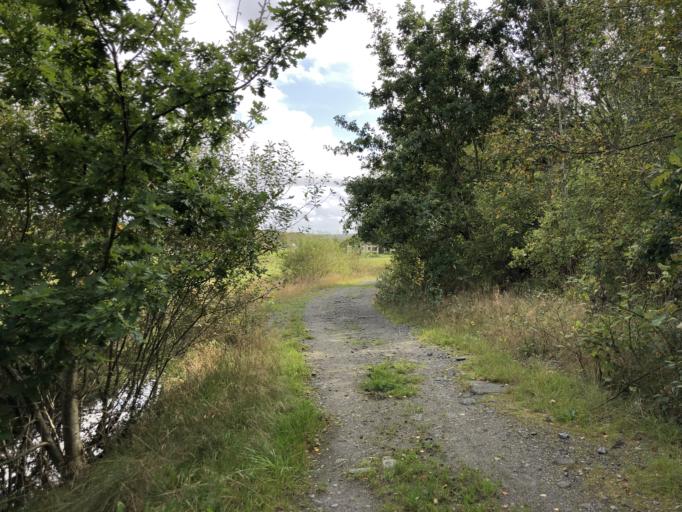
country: SE
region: Vaestra Goetaland
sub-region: Goteborg
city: Majorna
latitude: 57.7629
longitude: 11.8739
